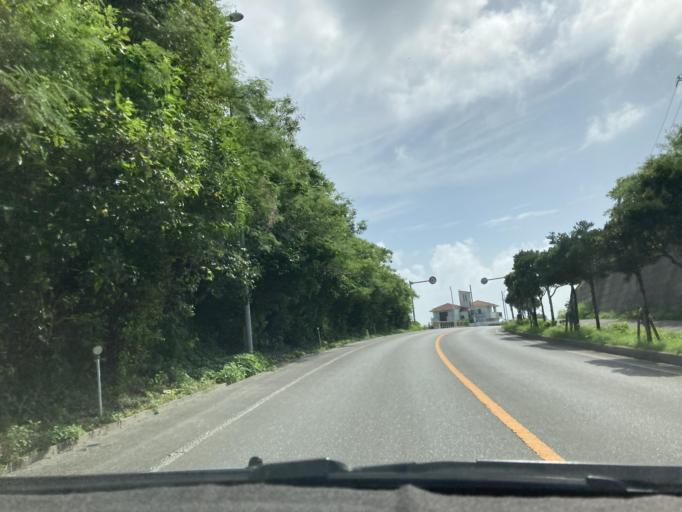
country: JP
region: Okinawa
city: Tomigusuku
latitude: 26.1433
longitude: 127.7955
